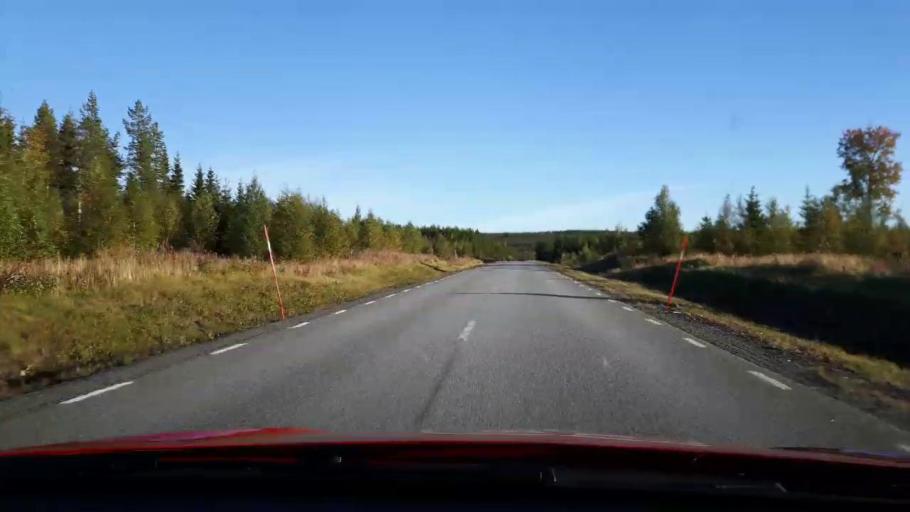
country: SE
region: Jaemtland
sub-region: OEstersunds Kommun
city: Lit
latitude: 63.7723
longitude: 14.7161
